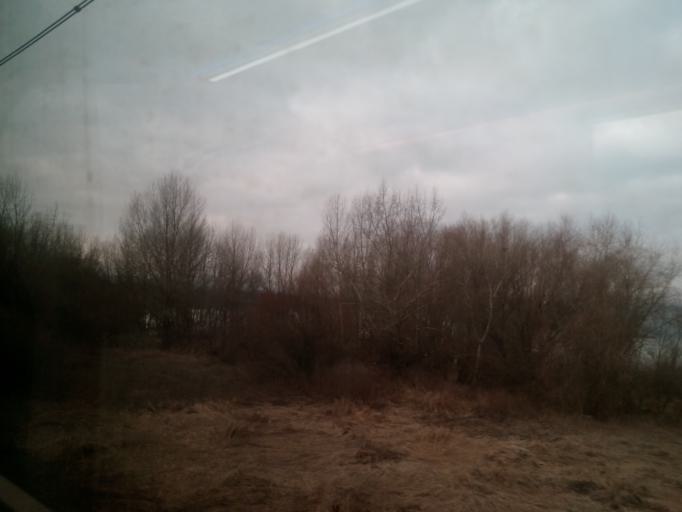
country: SK
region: Zilinsky
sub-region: Okres Liptovsky Mikulas
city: Liptovsky Mikulas
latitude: 49.0914
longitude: 19.5857
